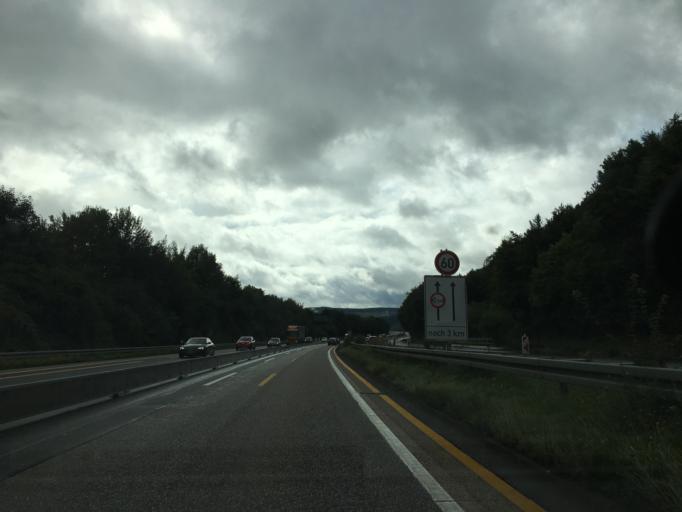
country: DE
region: North Rhine-Westphalia
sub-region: Regierungsbezirk Arnsberg
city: Siegen
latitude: 50.8579
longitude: 7.9855
